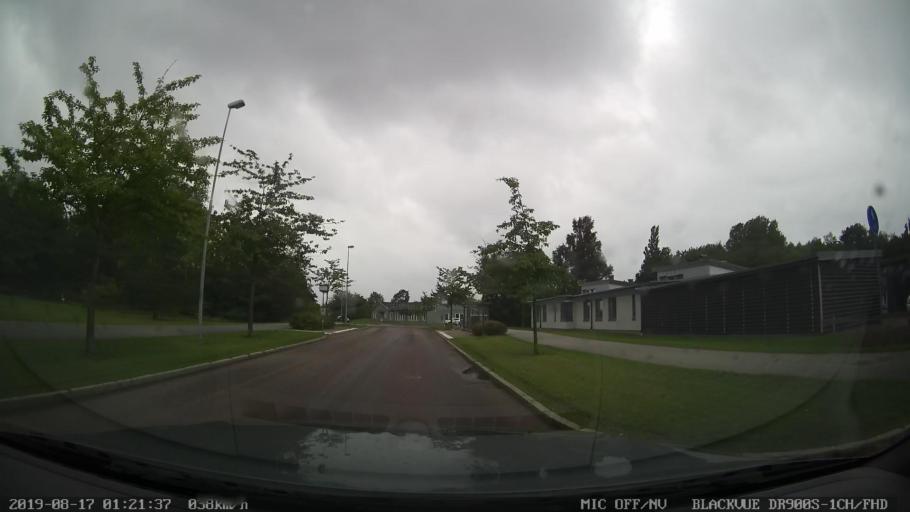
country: SE
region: Skane
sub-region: Landskrona
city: Landskrona
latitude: 55.8922
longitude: 12.8247
